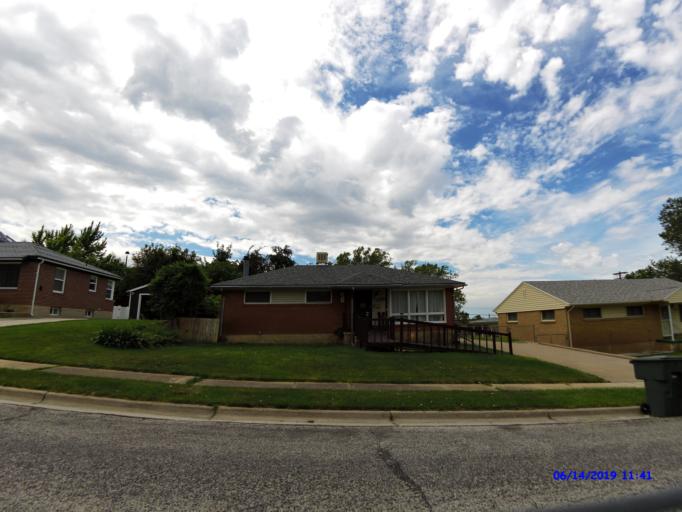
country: US
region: Utah
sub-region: Weber County
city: Ogden
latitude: 41.2523
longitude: -111.9450
